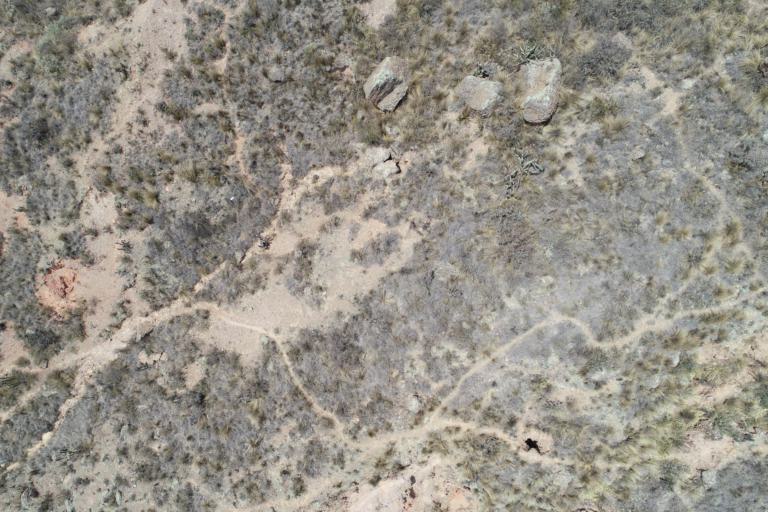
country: BO
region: La Paz
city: La Paz
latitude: -16.5579
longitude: -68.0918
